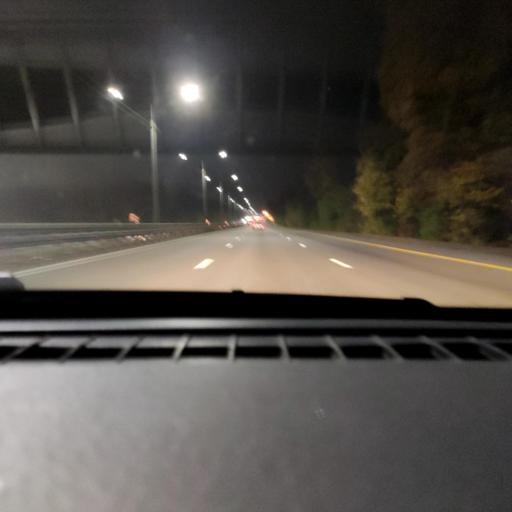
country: RU
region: Voronezj
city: Podgornoye
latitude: 51.8148
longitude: 39.2074
